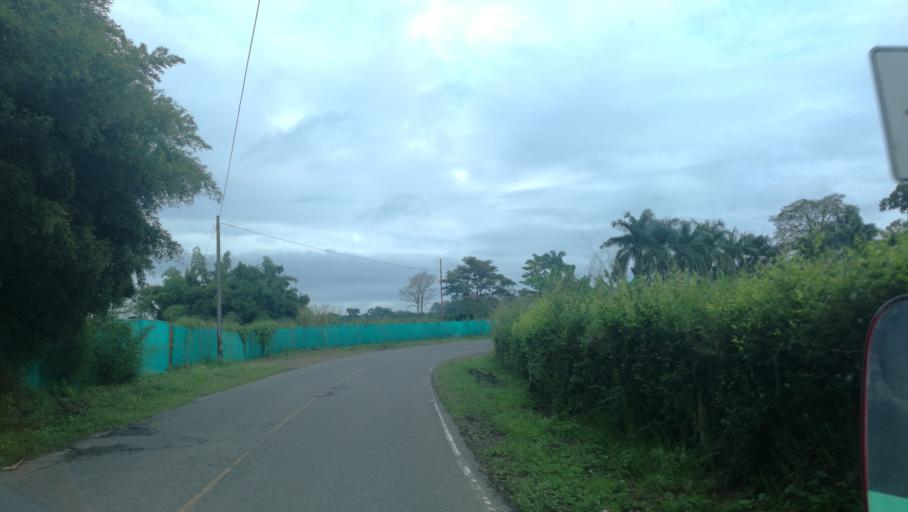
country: CO
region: Quindio
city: Montenegro
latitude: 4.5366
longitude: -75.7760
